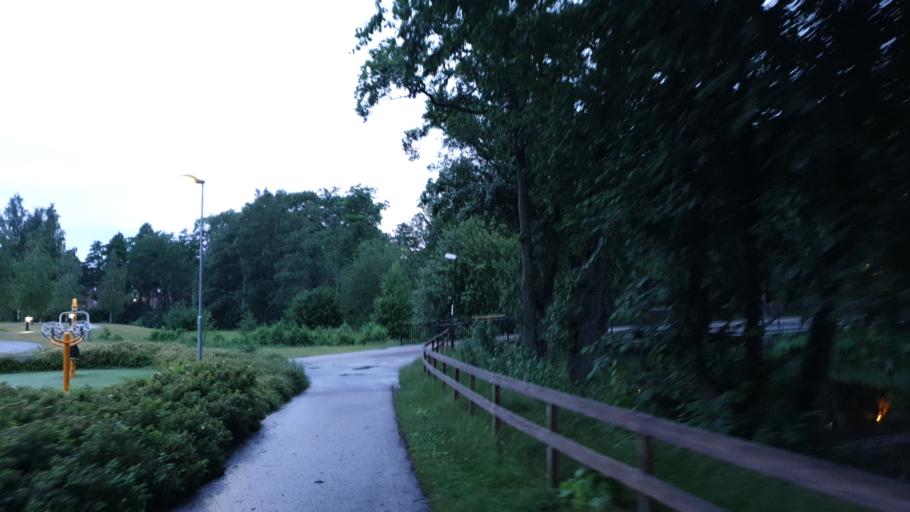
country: SE
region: Kronoberg
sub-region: Ljungby Kommun
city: Ljungby
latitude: 56.8287
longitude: 13.9420
